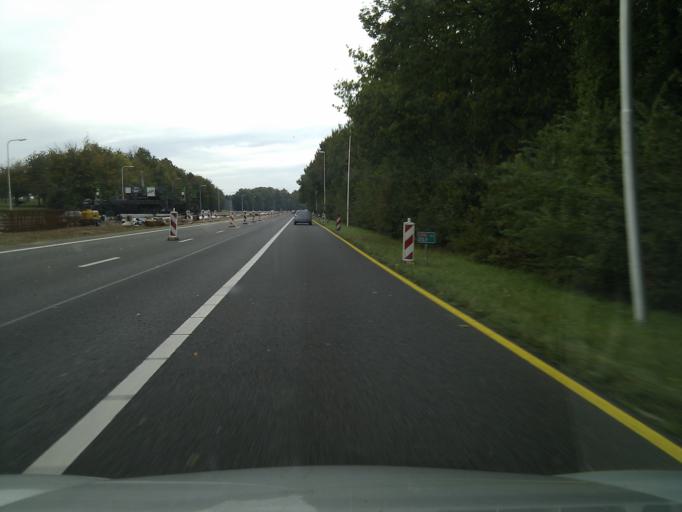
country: NL
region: Limburg
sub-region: Gemeente Simpelveld
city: Simpelveld
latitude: 50.8455
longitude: 5.9886
